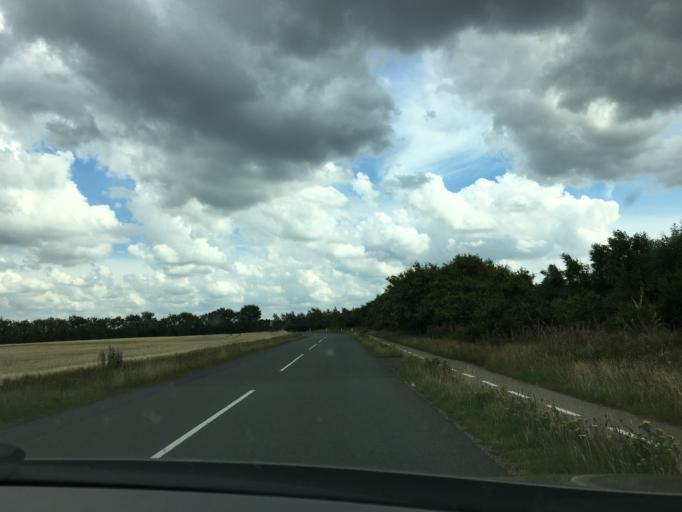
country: DK
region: Central Jutland
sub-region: Ringkobing-Skjern Kommune
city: Skjern
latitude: 55.9493
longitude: 8.4122
